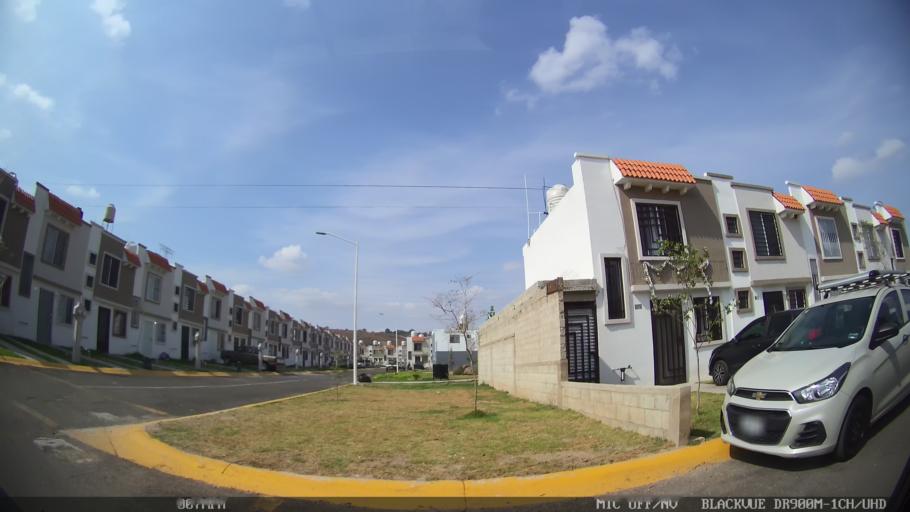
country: MX
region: Jalisco
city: Tonala
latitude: 20.6461
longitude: -103.2297
